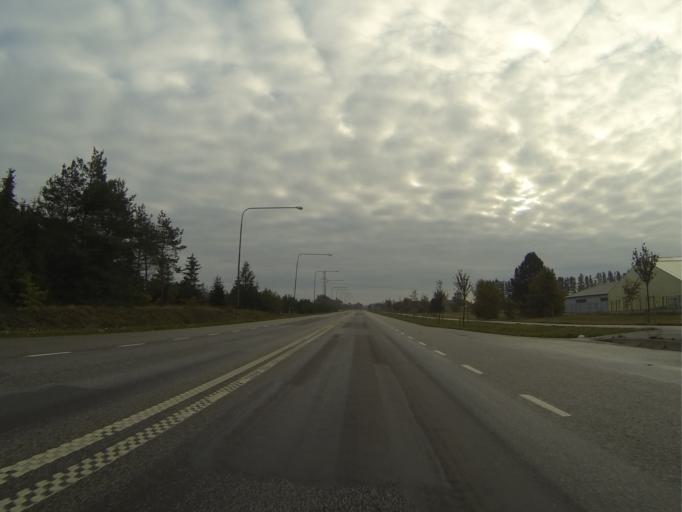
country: SE
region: Skane
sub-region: Tomelilla Kommun
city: Tomelilla
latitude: 55.5589
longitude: 13.9193
